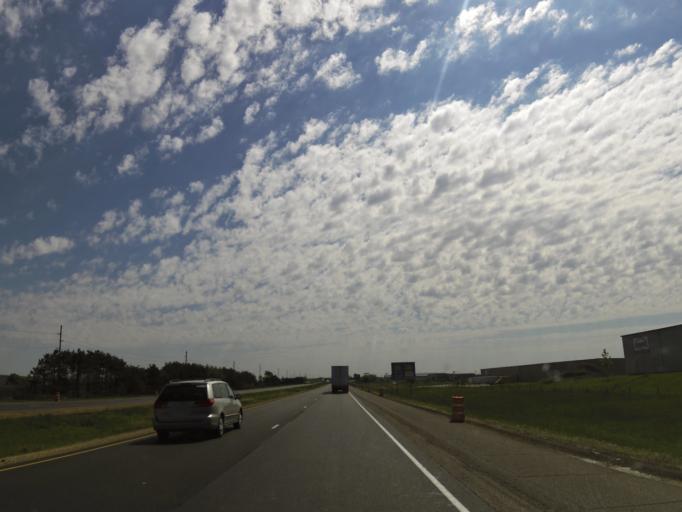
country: US
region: Wisconsin
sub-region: Dunn County
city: Menomonie
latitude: 44.9046
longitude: -91.8697
